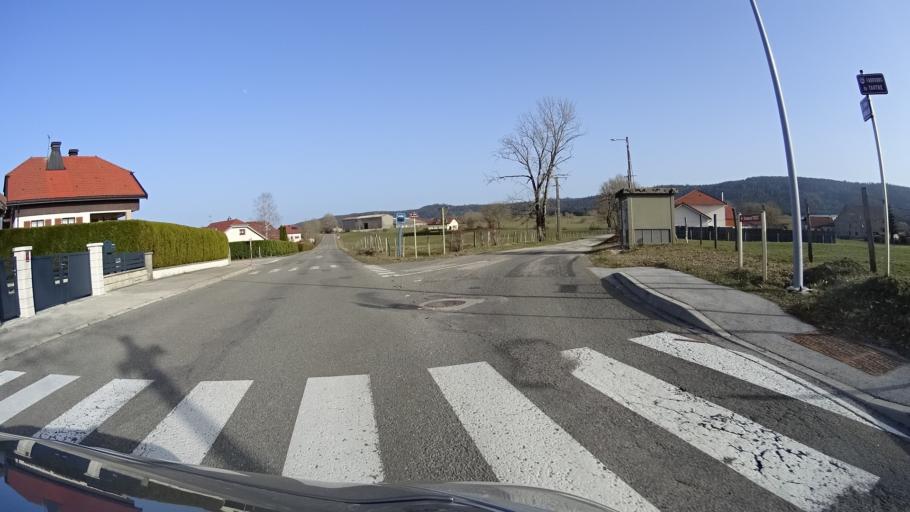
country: FR
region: Franche-Comte
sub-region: Departement du Doubs
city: Frasne
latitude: 46.8658
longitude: 6.2223
